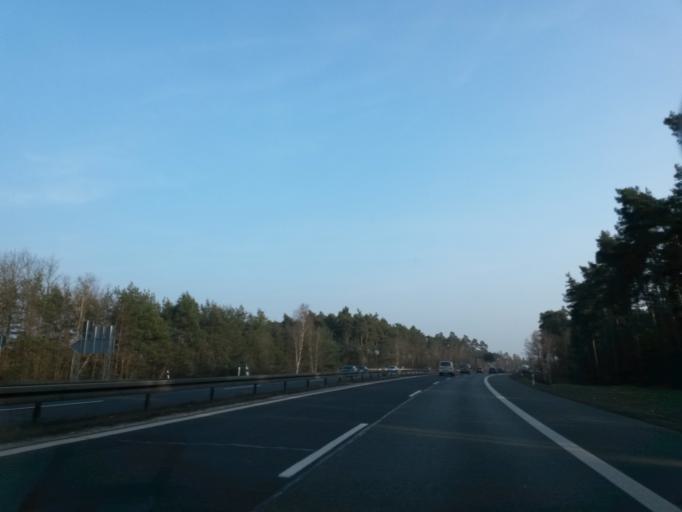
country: DE
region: Bavaria
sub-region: Regierungsbezirk Mittelfranken
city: Feucht
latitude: 49.3630
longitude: 11.1983
